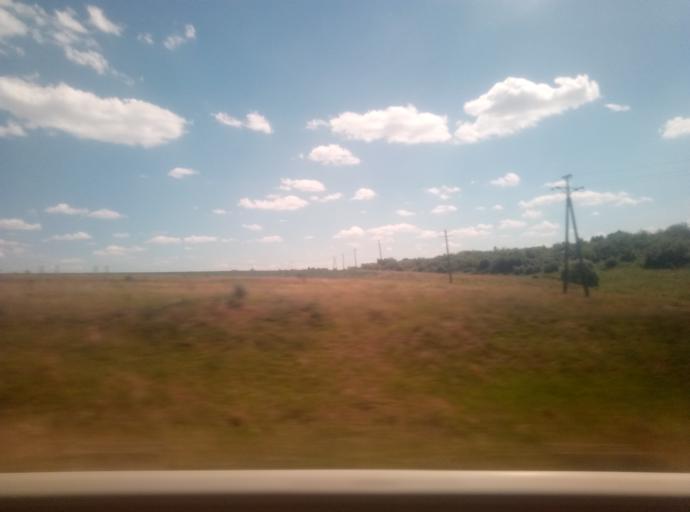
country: RU
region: Tula
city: Kireyevsk
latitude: 53.9390
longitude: 37.9482
